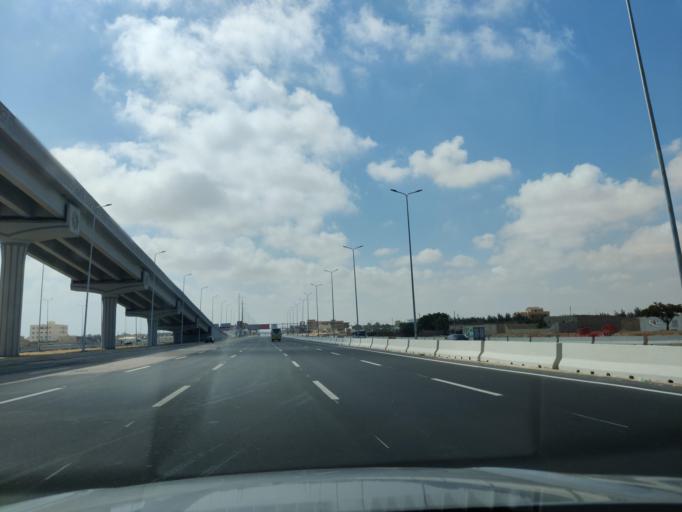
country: EG
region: Muhafazat Matruh
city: Al `Alamayn
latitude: 30.9511
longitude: 28.7716
